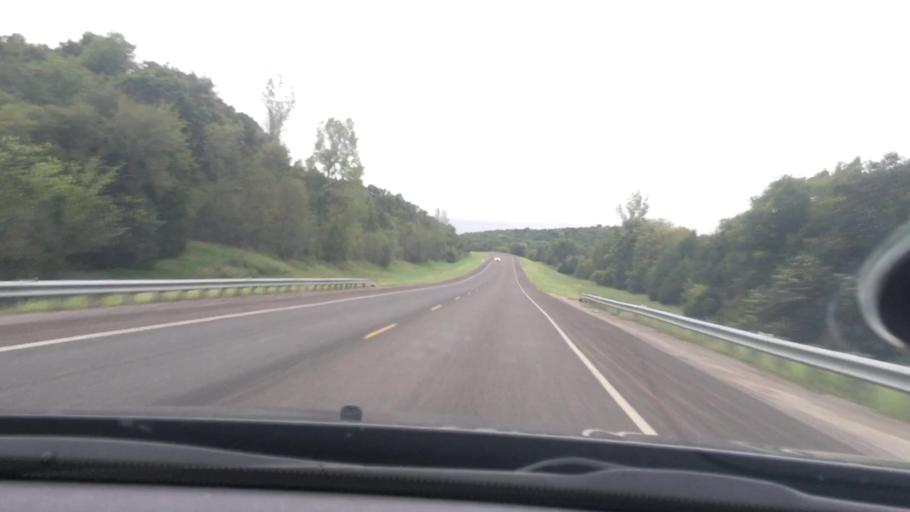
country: US
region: Oklahoma
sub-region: Sequoyah County
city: Vian
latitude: 35.5326
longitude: -94.9723
